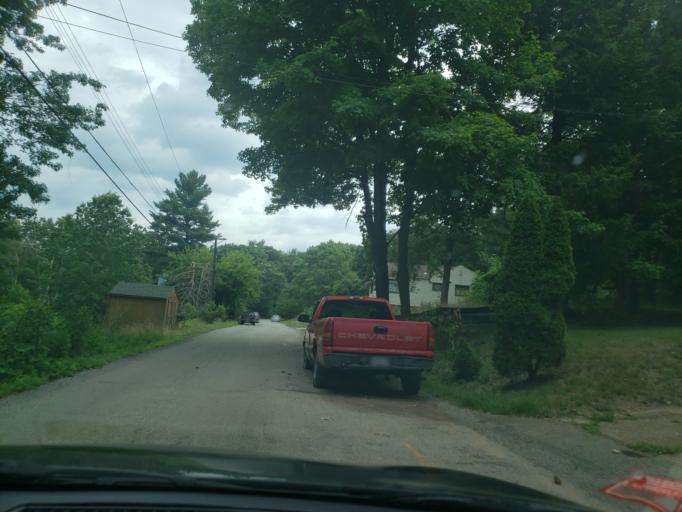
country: US
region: Pennsylvania
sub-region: Allegheny County
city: Emsworth
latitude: 40.5172
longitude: -80.0875
